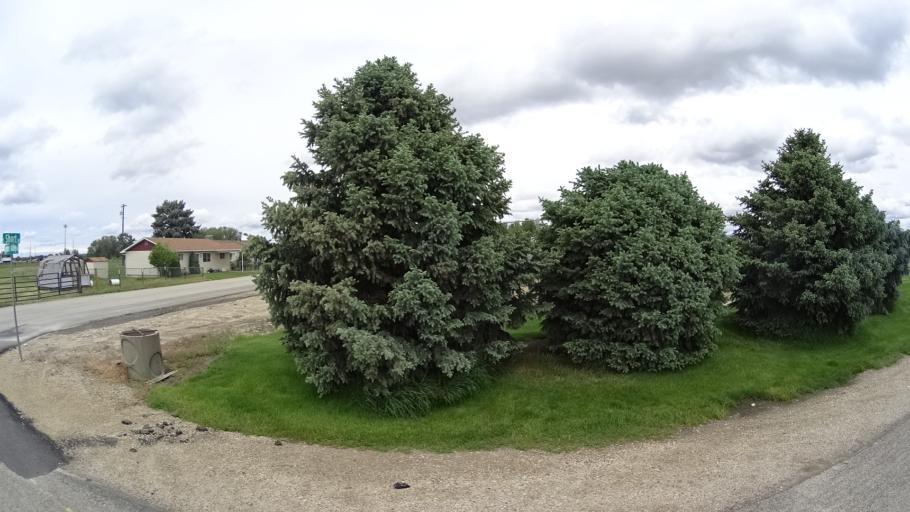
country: US
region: Idaho
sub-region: Ada County
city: Star
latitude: 43.6890
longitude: -116.4506
